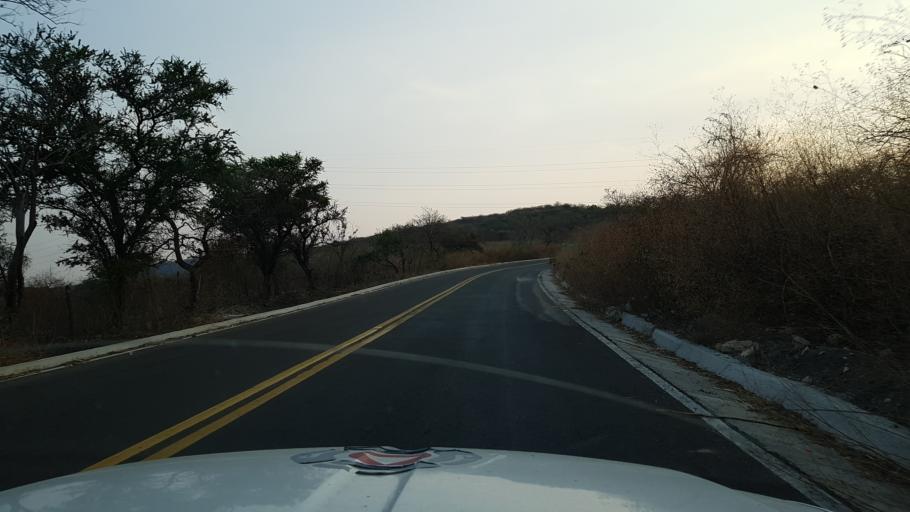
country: MX
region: Morelos
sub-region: Ayala
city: Olintepec
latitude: 18.7340
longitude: -99.0121
